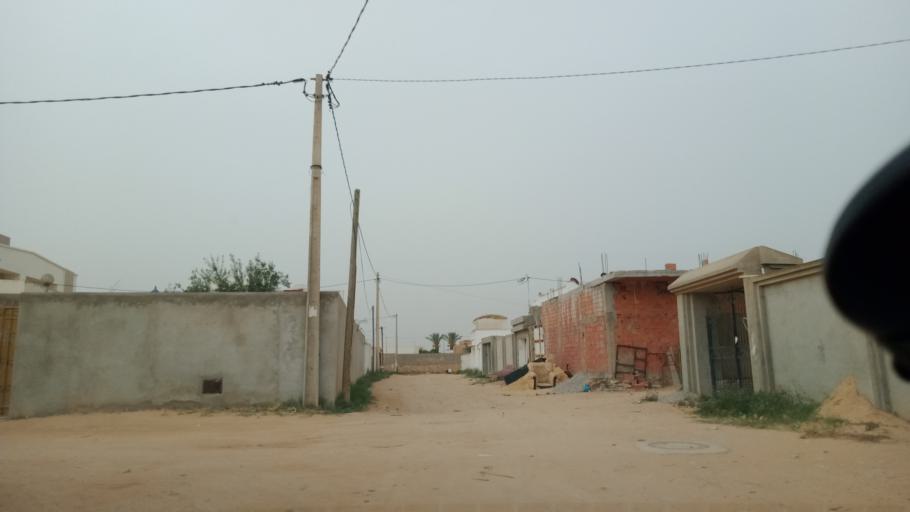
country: TN
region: Safaqis
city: Al Qarmadah
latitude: 34.7914
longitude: 10.7656
